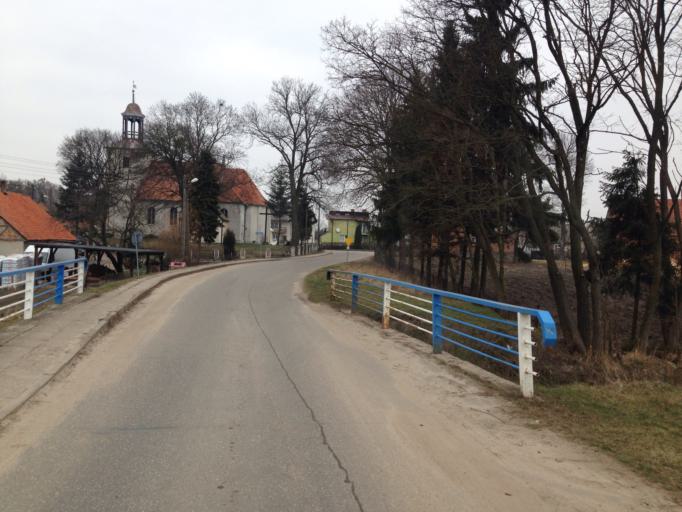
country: PL
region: Pomeranian Voivodeship
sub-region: Powiat kwidzynski
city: Sadlinki
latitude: 53.7411
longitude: 18.8241
